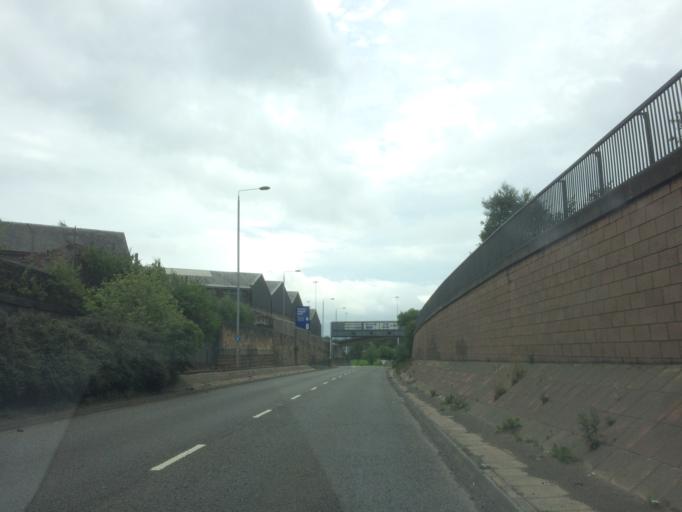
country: GB
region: Scotland
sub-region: Glasgow City
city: Glasgow
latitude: 55.8716
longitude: -4.2336
